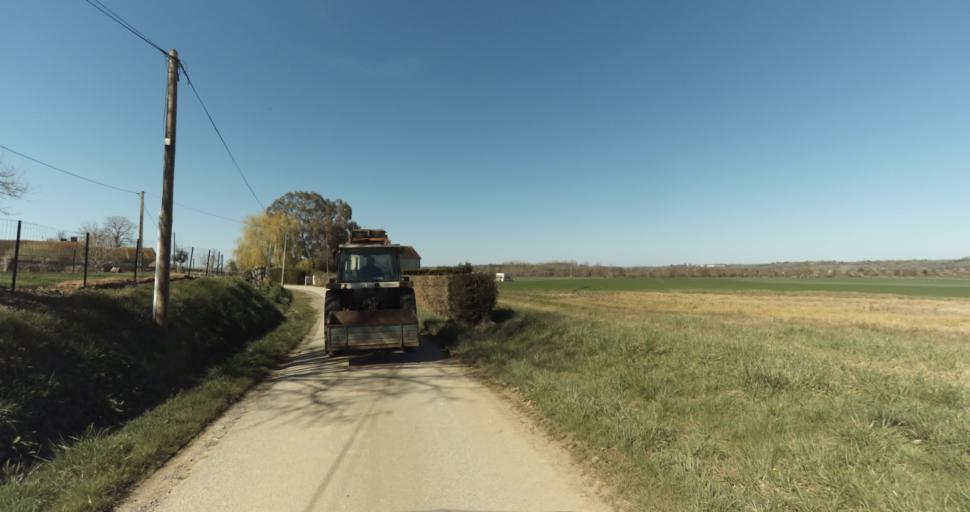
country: FR
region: Lower Normandy
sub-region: Departement du Calvados
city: Saint-Pierre-sur-Dives
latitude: 49.0372
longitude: -0.0065
